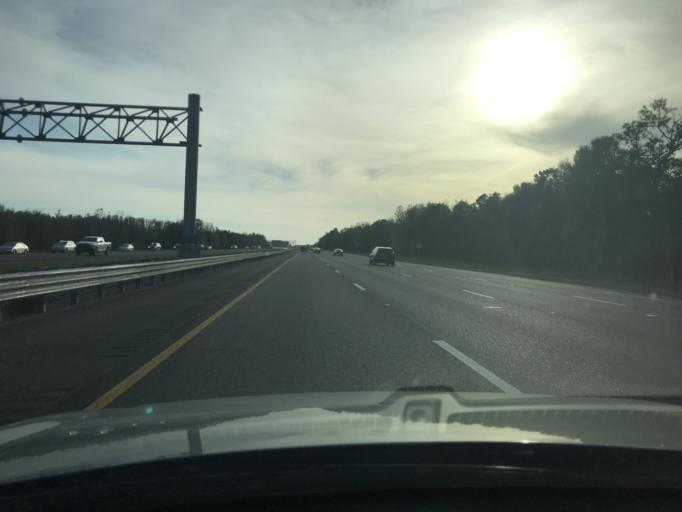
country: US
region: Florida
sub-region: Pasco County
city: Wesley Chapel
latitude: 28.2279
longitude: -82.3617
